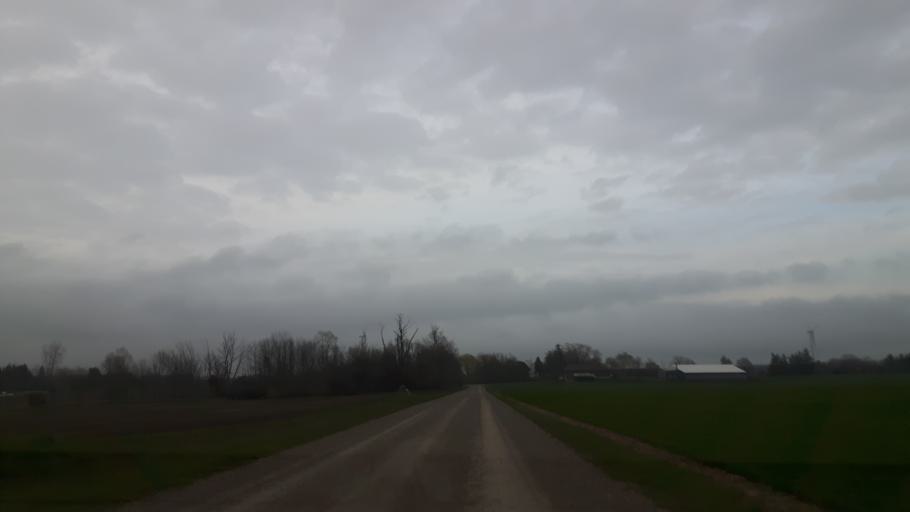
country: CA
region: Ontario
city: Bluewater
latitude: 43.5088
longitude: -81.6733
